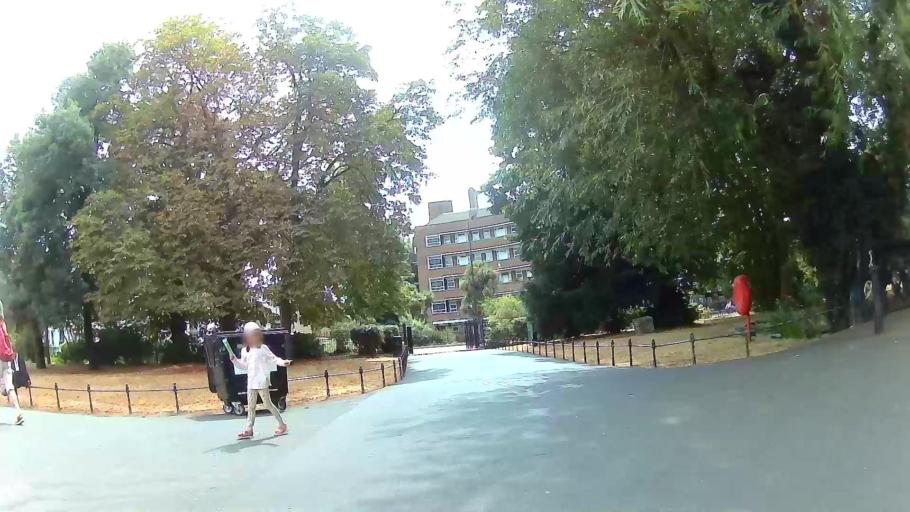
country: GB
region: England
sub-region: Greater London
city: Harringay
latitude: 51.5606
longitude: -0.0862
